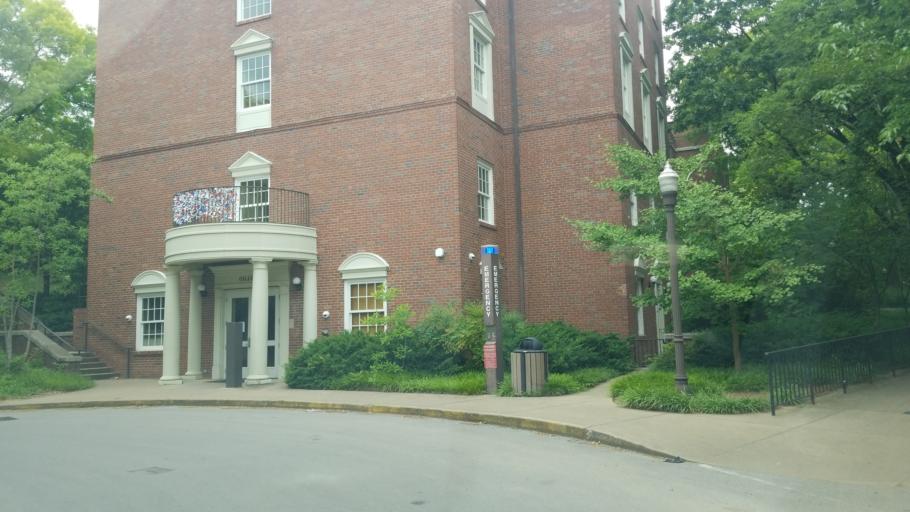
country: US
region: Tennessee
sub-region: Davidson County
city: Nashville
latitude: 36.1411
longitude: -86.7977
